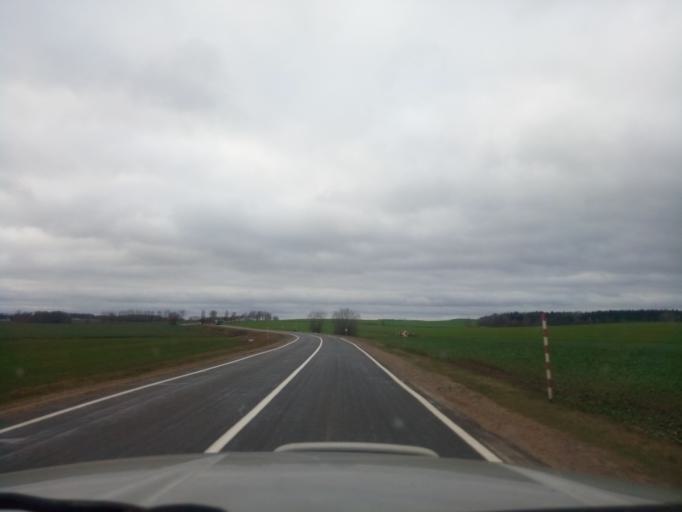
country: BY
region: Minsk
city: Kapyl'
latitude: 53.1891
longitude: 27.1848
